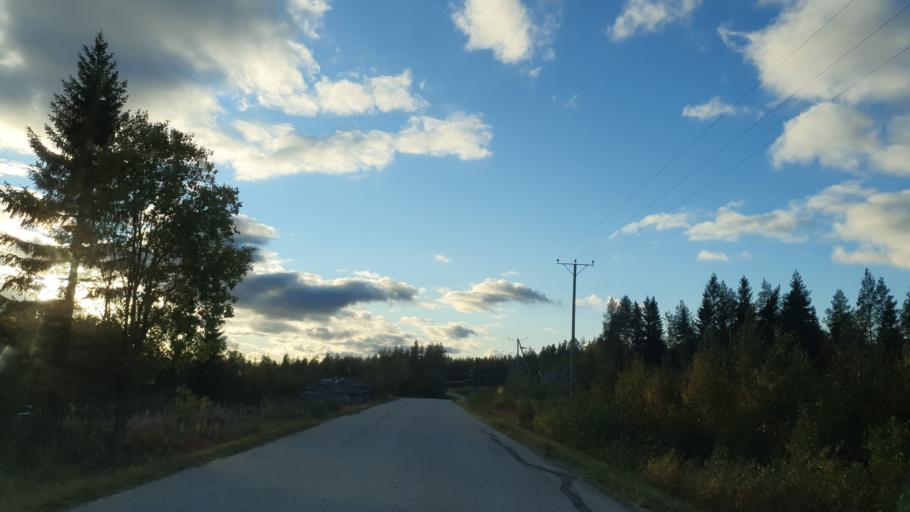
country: FI
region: Kainuu
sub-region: Kehys-Kainuu
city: Kuhmo
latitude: 63.9538
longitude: 29.7385
